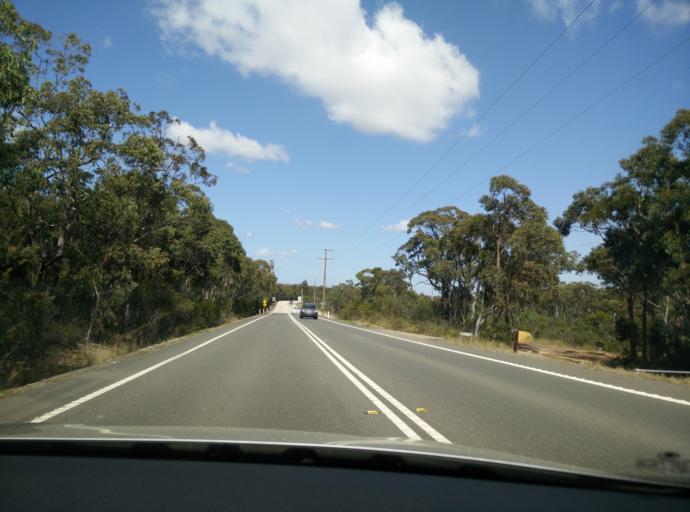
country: AU
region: New South Wales
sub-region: Gosford Shire
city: Point Clare
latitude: -33.4560
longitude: 151.2858
